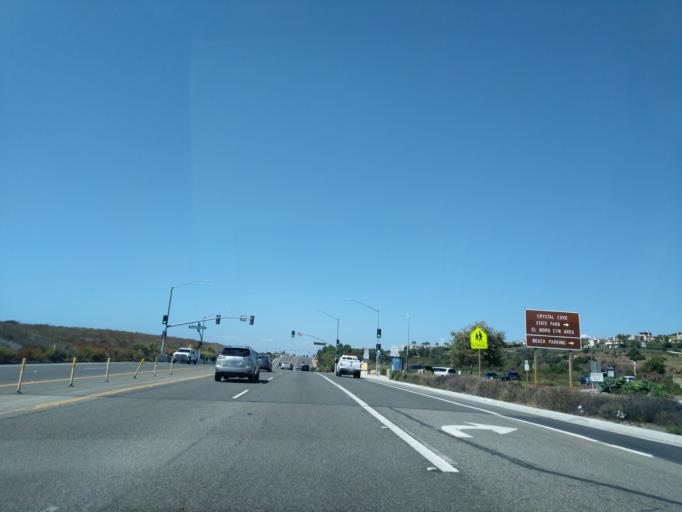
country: US
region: California
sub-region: Orange County
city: Laguna Beach
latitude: 33.5637
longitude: -117.8251
